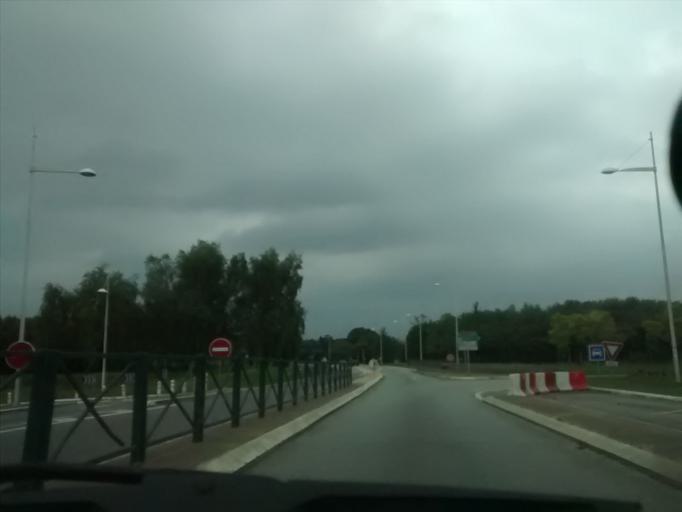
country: FR
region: Brittany
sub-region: Departement du Morbihan
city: Guer
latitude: 47.9305
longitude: -2.1274
